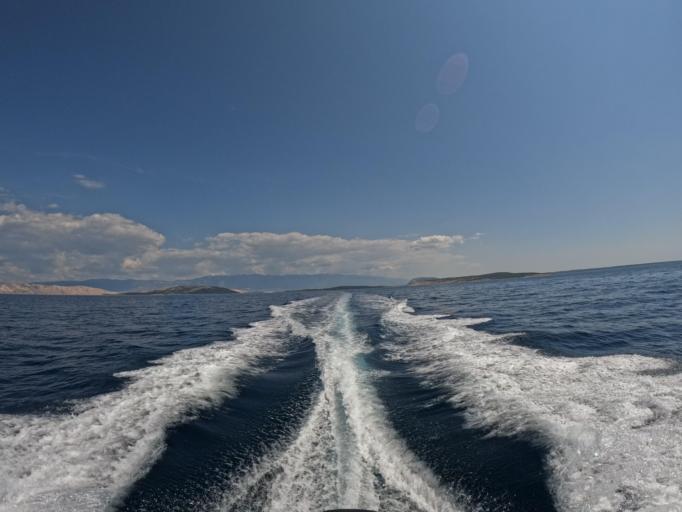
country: HR
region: Primorsko-Goranska
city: Lopar
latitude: 44.8740
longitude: 14.6658
